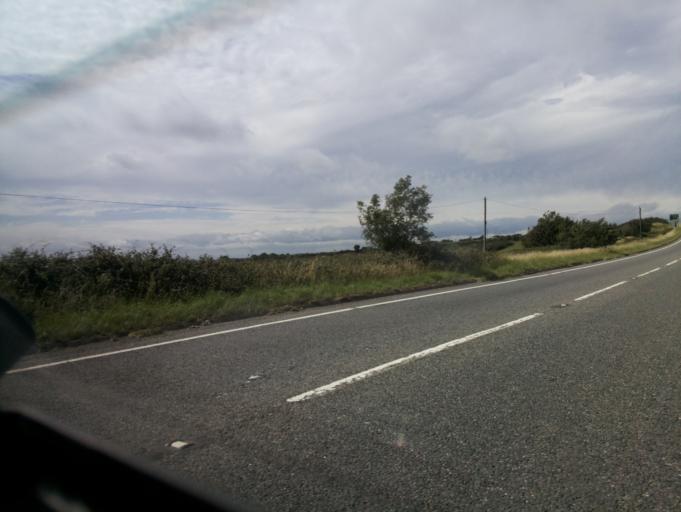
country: GB
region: England
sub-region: Dorset
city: Dorchester
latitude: 50.8001
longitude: -2.5499
